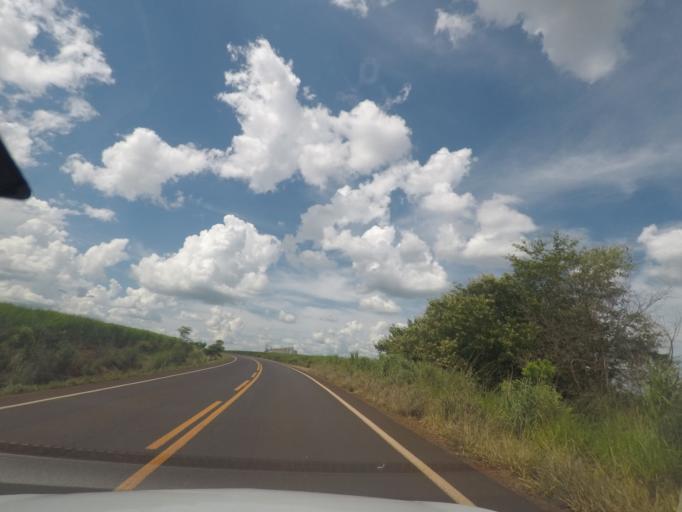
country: BR
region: Minas Gerais
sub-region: Conceicao Das Alagoas
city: Conceicao das Alagoas
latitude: -19.8124
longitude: -48.5845
